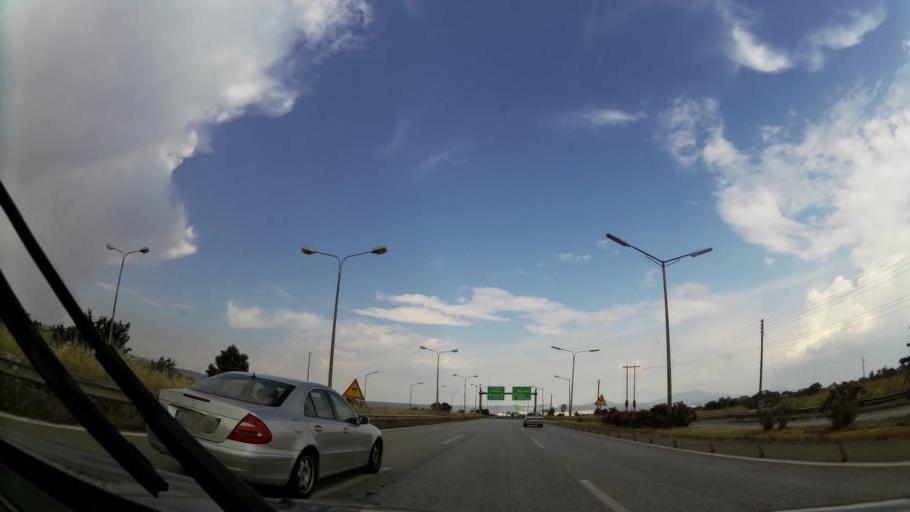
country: GR
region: Central Macedonia
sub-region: Nomos Thessalonikis
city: Kalochori
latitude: 40.6521
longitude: 22.8296
